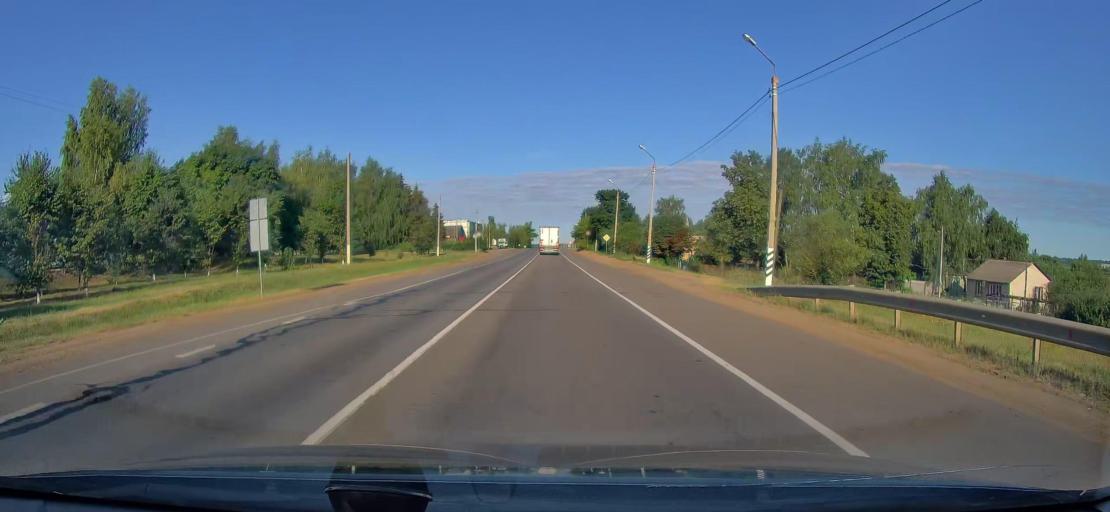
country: RU
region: Tula
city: Chern'
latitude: 53.4555
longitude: 36.9258
